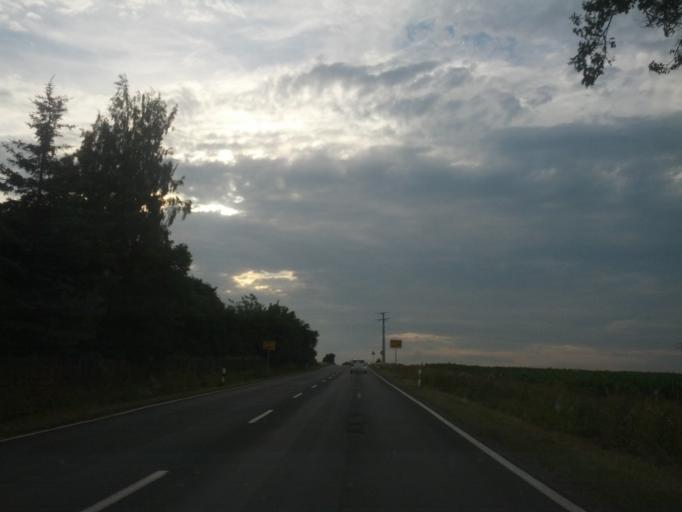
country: DE
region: Thuringia
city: Ingersleben
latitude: 50.9572
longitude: 10.9658
